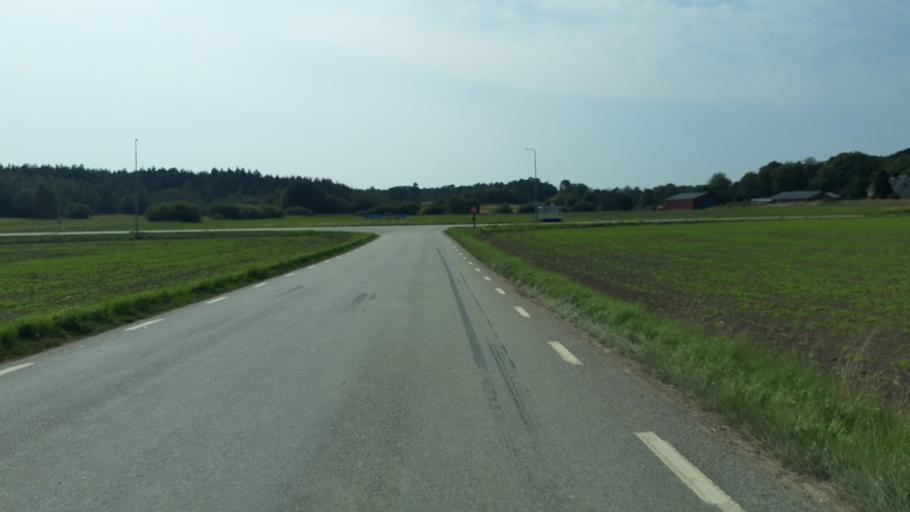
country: SE
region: Blekinge
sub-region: Ronneby Kommun
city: Ronneby
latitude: 56.1961
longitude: 15.3395
